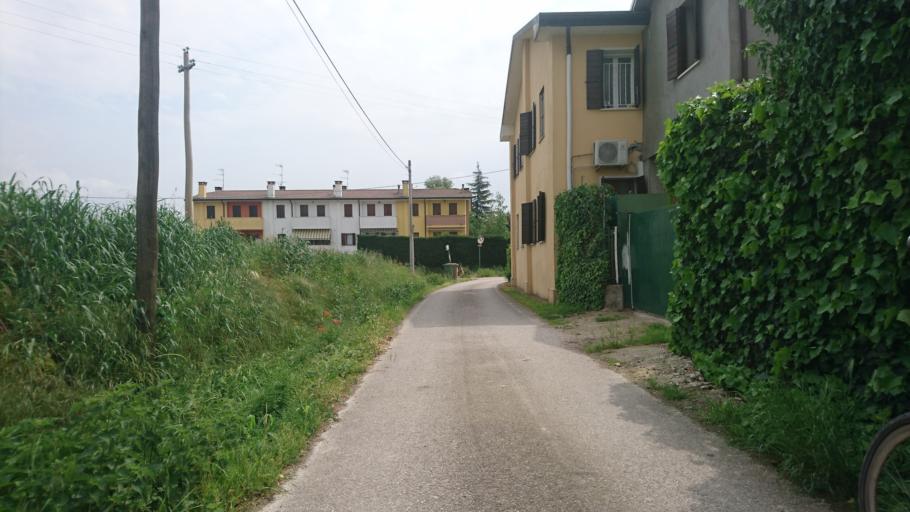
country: IT
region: Veneto
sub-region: Provincia di Padova
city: Monselice
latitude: 45.2165
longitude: 11.7320
